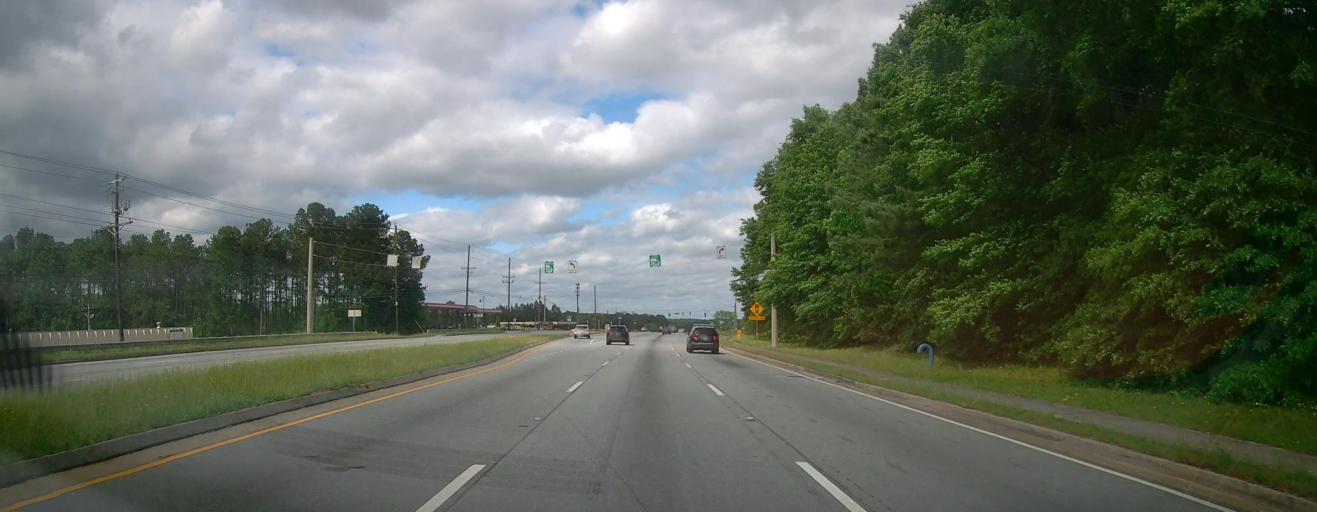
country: US
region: Georgia
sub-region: Rockdale County
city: Conyers
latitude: 33.6678
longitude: -83.9894
